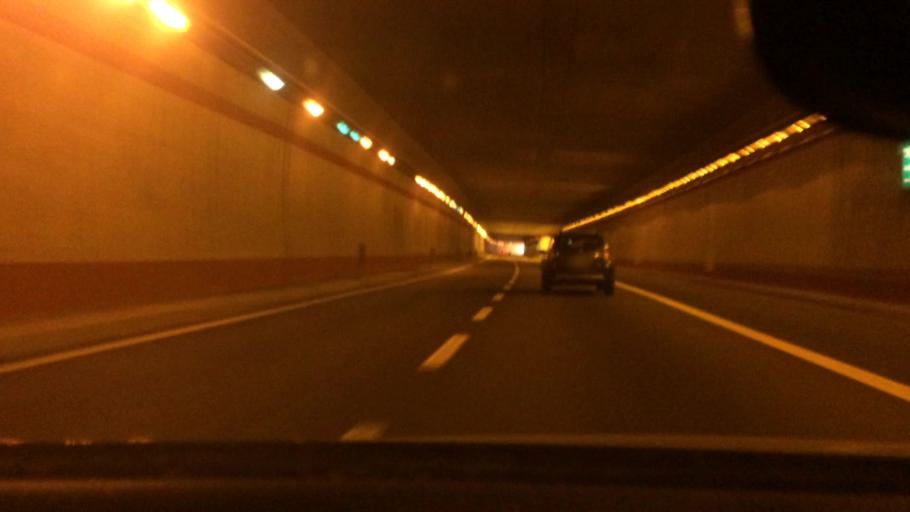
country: IT
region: Lombardy
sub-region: Citta metropolitana di Milano
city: Buscate
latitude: 45.5498
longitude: 8.7949
